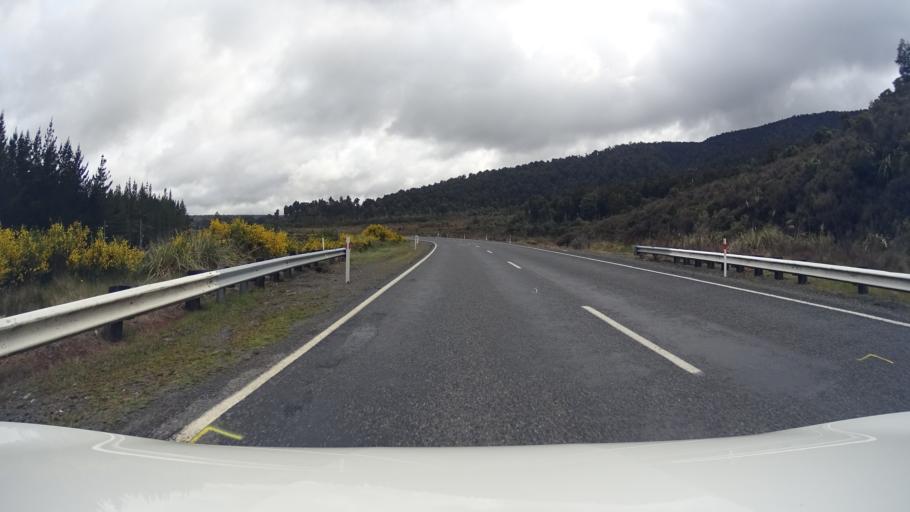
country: NZ
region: Manawatu-Wanganui
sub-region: Ruapehu District
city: Waiouru
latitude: -39.2224
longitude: 175.3991
